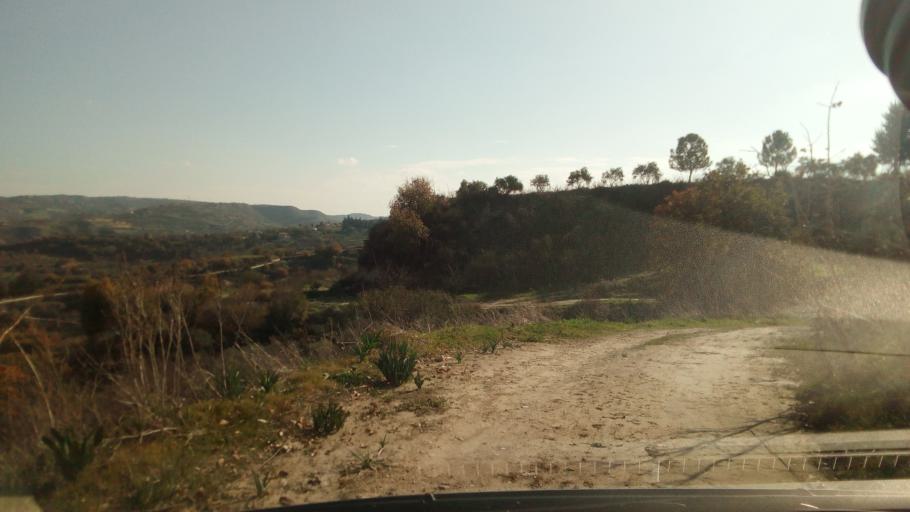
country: CY
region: Pafos
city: Pegeia
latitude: 34.9317
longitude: 32.4613
